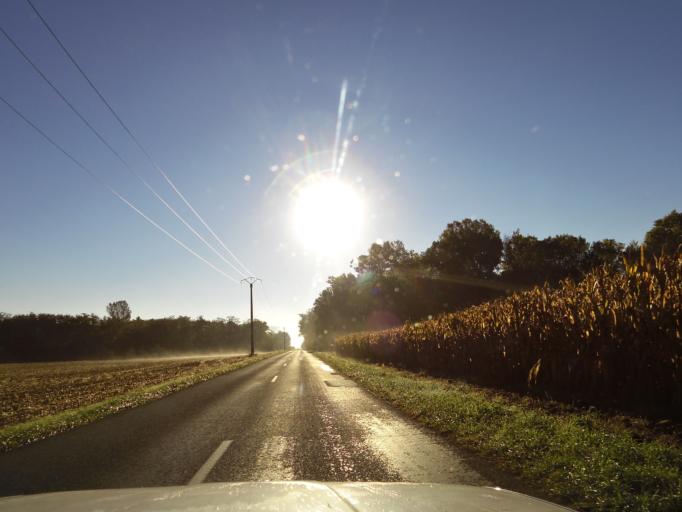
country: FR
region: Rhone-Alpes
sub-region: Departement de l'Ain
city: Leyment
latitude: 45.8834
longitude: 5.2975
